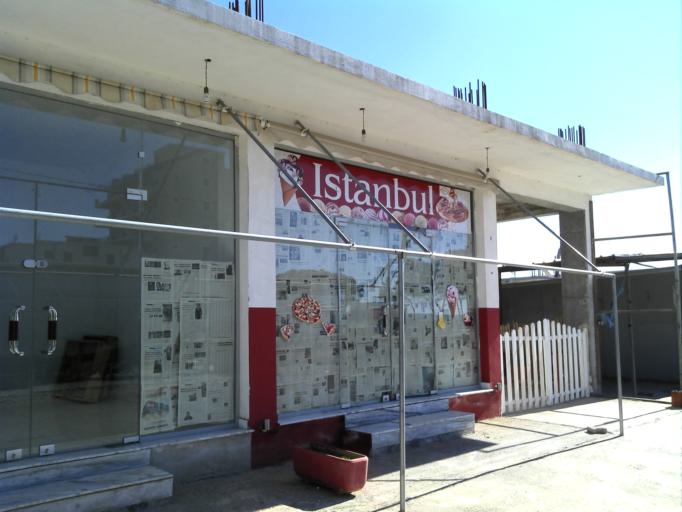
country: AL
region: Shkoder
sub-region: Rrethi i Shkodres
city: Velipoje
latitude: 41.8634
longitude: 19.4224
